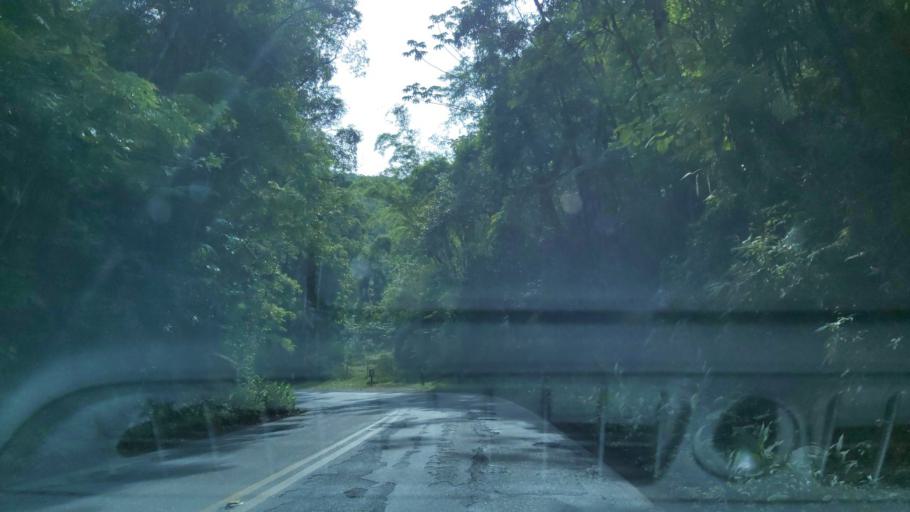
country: BR
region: Sao Paulo
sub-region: Miracatu
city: Miracatu
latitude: -24.0543
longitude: -47.5716
